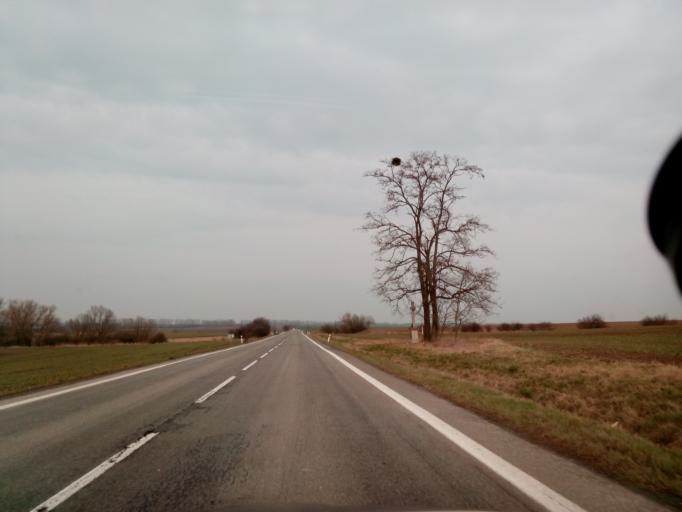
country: SK
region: Kosicky
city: Trebisov
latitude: 48.5299
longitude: 21.6716
